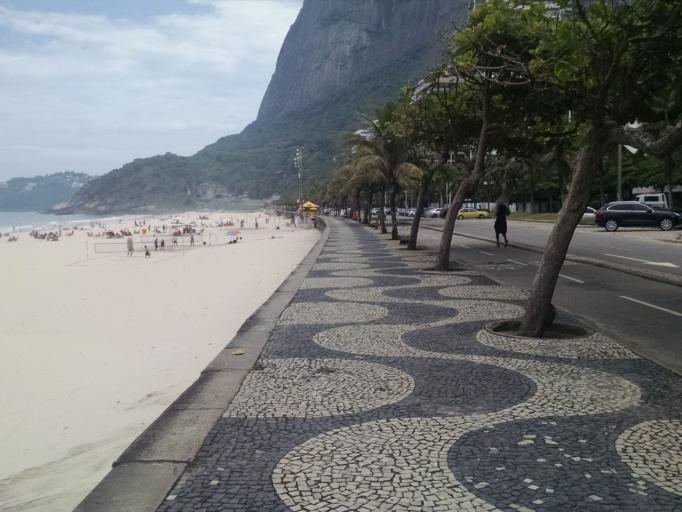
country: BR
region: Rio de Janeiro
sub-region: Rio De Janeiro
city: Rio de Janeiro
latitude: -22.9998
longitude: -43.2675
